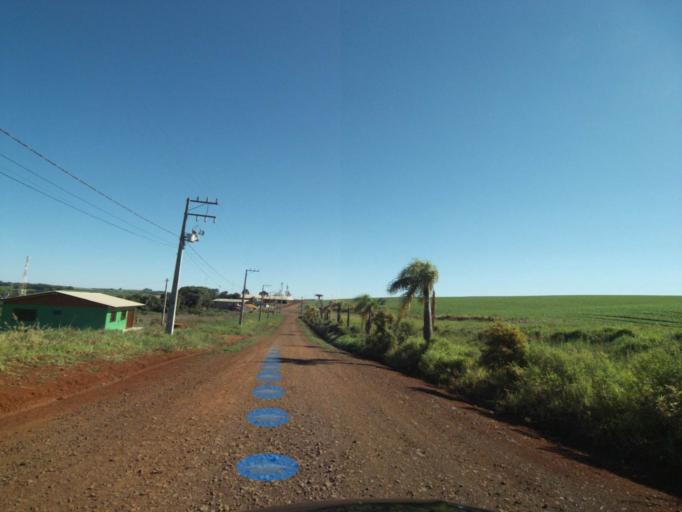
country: BR
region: Parana
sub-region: Coronel Vivida
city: Coronel Vivida
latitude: -26.1371
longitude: -52.3936
